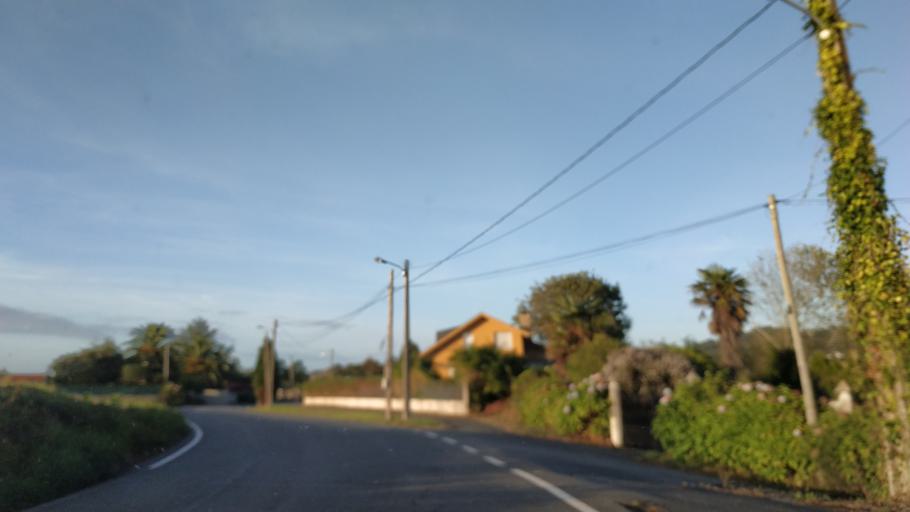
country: ES
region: Galicia
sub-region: Provincia da Coruna
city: Oleiros
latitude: 43.3595
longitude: -8.3426
